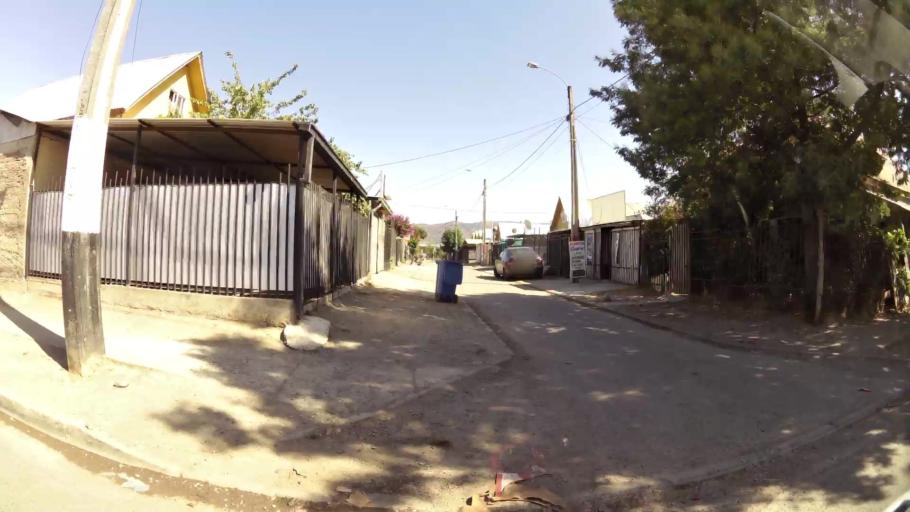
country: CL
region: Maule
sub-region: Provincia de Talca
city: Talca
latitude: -35.4052
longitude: -71.6487
